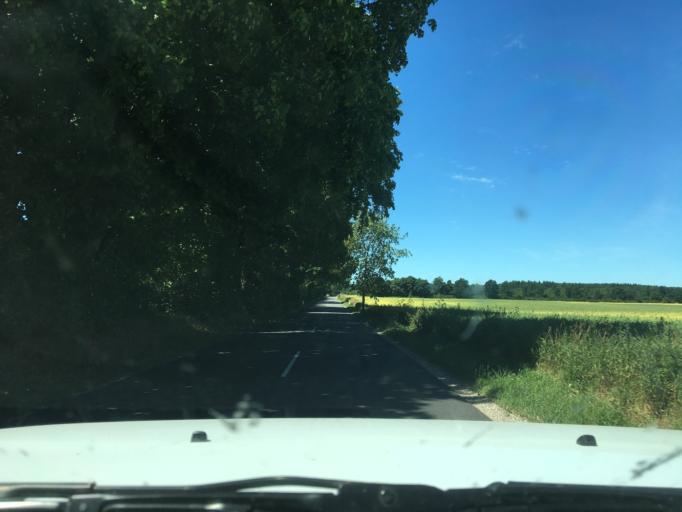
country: DK
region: Central Jutland
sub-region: Syddjurs Kommune
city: Hornslet
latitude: 56.3284
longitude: 10.3507
